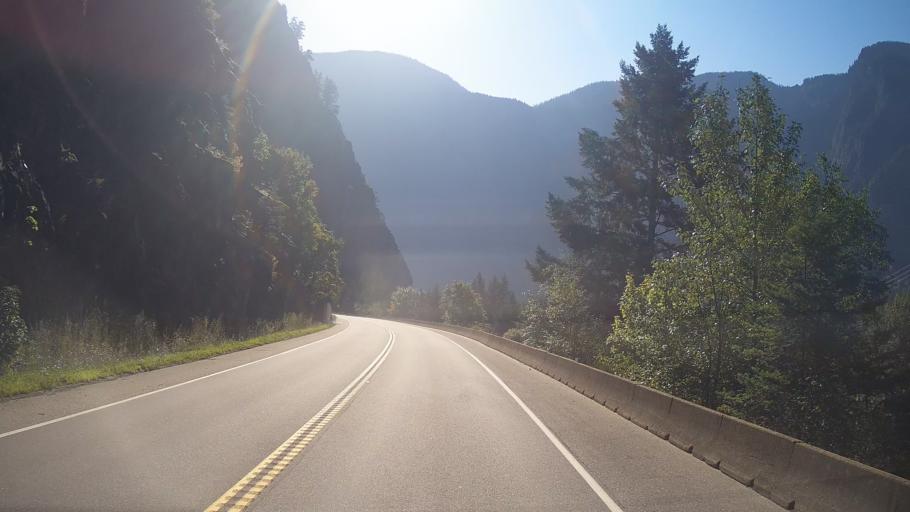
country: CA
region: British Columbia
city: Hope
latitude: 49.5633
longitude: -121.4200
